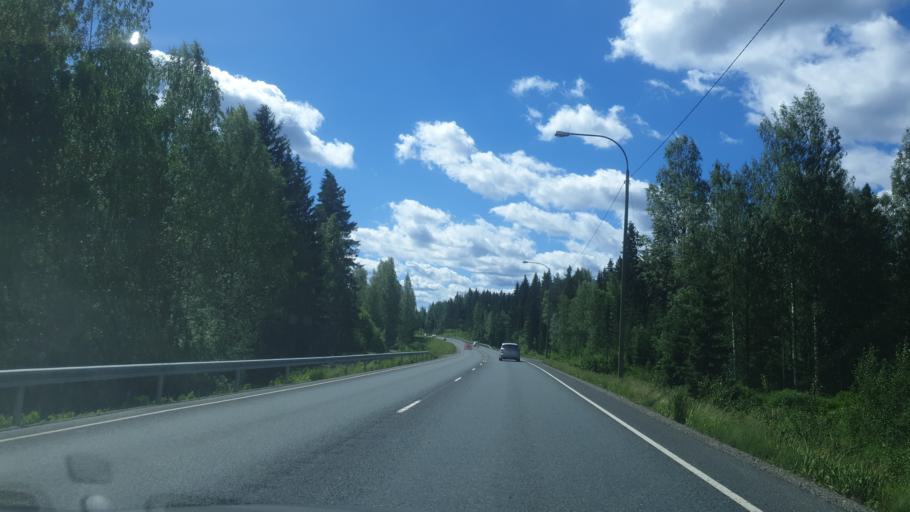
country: FI
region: Northern Savo
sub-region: Varkaus
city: Leppaevirta
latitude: 62.6001
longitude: 27.6111
